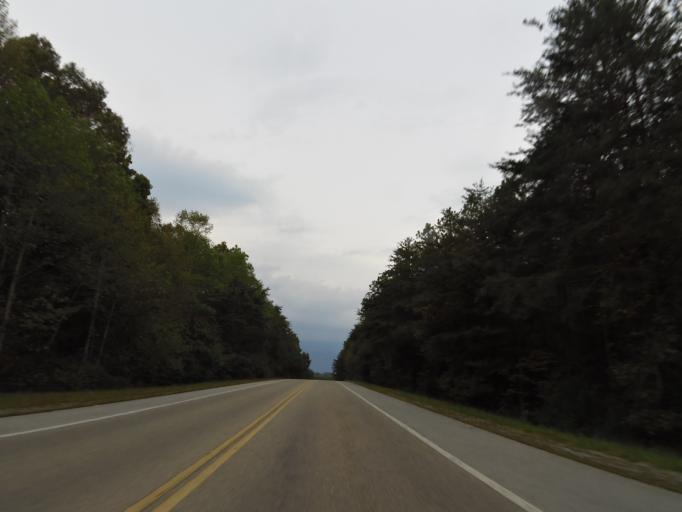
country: US
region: Tennessee
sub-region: Loudon County
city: Loudon
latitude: 35.6847
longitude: -84.2631
